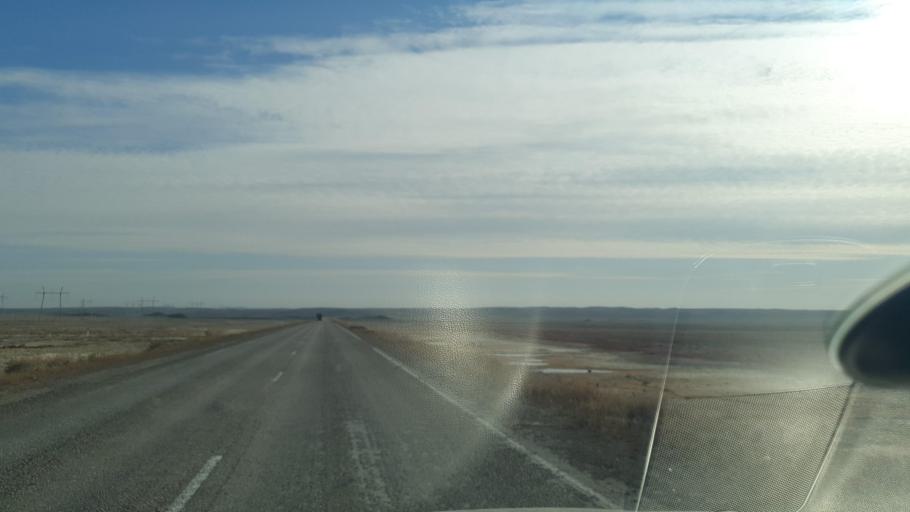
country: KZ
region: Zhambyl
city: Mynaral
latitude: 45.5741
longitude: 73.4144
